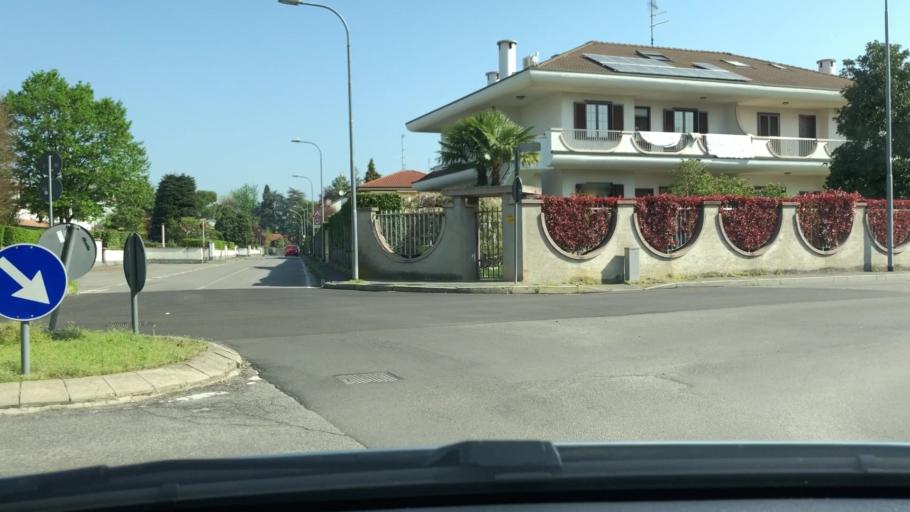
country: IT
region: Lombardy
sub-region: Provincia di Monza e Brianza
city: Barlassina
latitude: 45.6448
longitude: 9.1286
